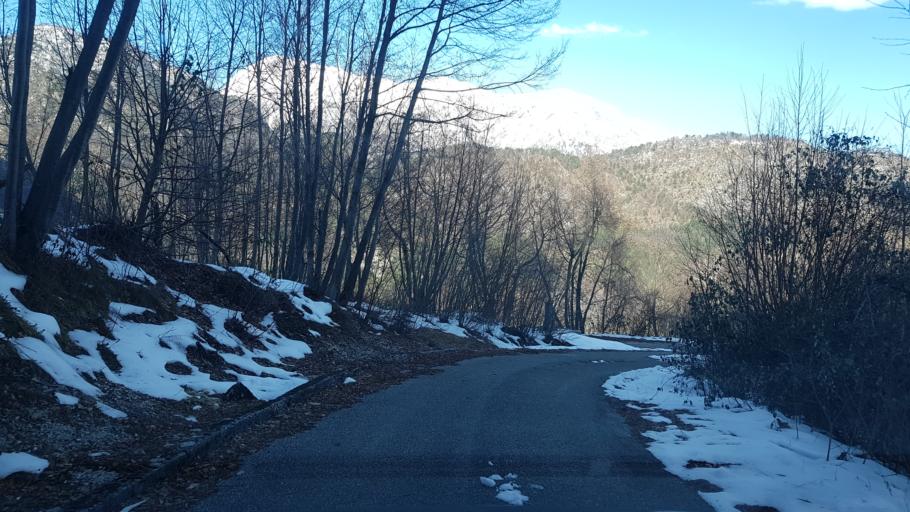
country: IT
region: Friuli Venezia Giulia
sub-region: Provincia di Udine
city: Trasaghis
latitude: 46.2938
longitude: 13.0277
